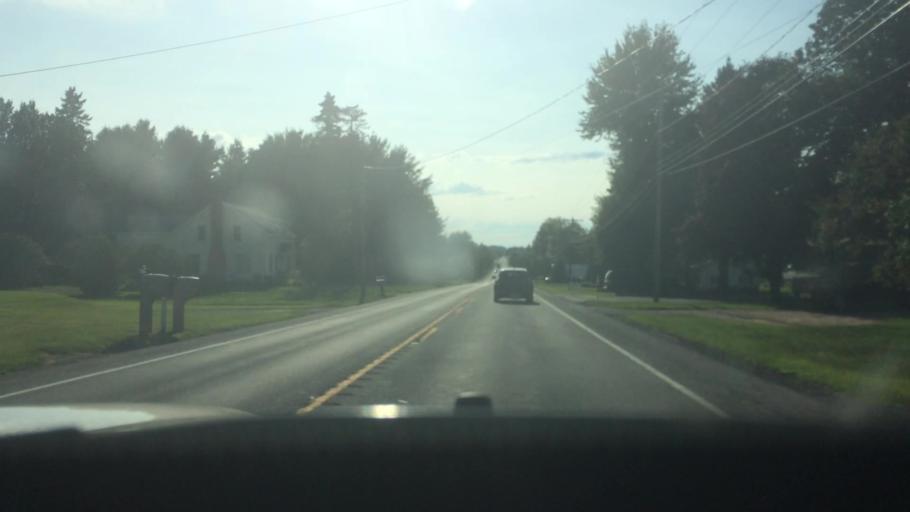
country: US
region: New York
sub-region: St. Lawrence County
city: Potsdam
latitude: 44.6701
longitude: -74.9374
